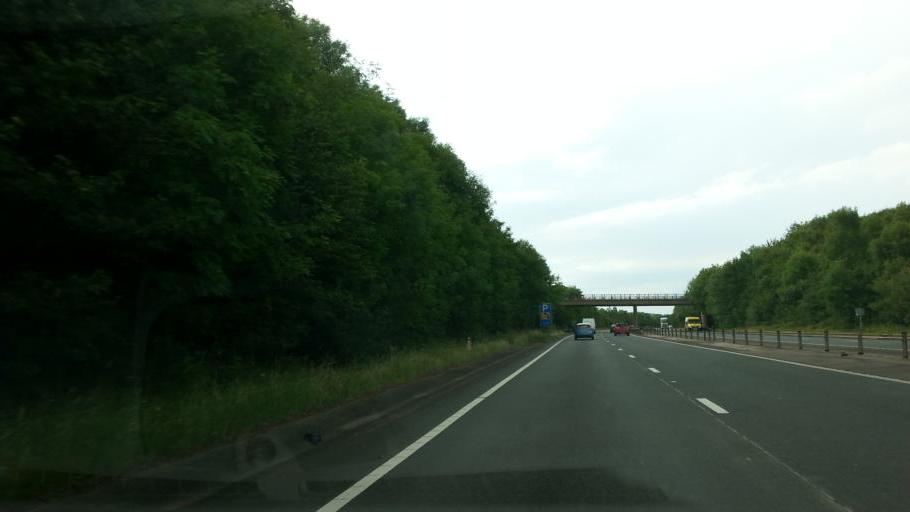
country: GB
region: Wales
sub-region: Monmouthshire
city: Llanbadoc
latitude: 51.6875
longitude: -2.8784
